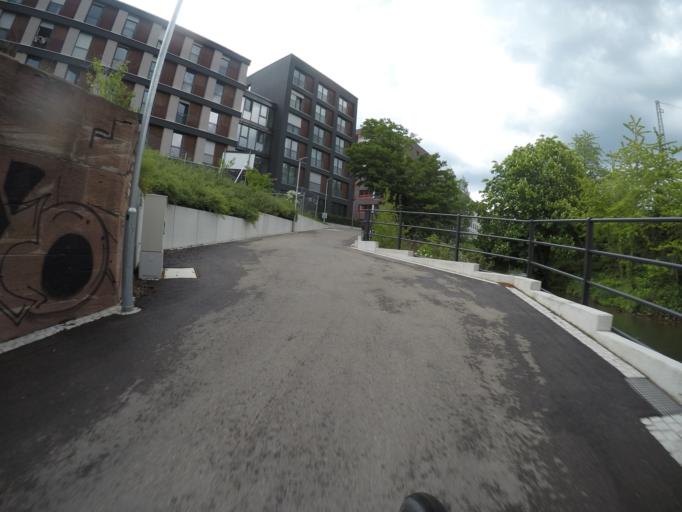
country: DE
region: Baden-Wuerttemberg
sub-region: Regierungsbezirk Stuttgart
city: Esslingen
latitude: 48.7414
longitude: 9.2893
